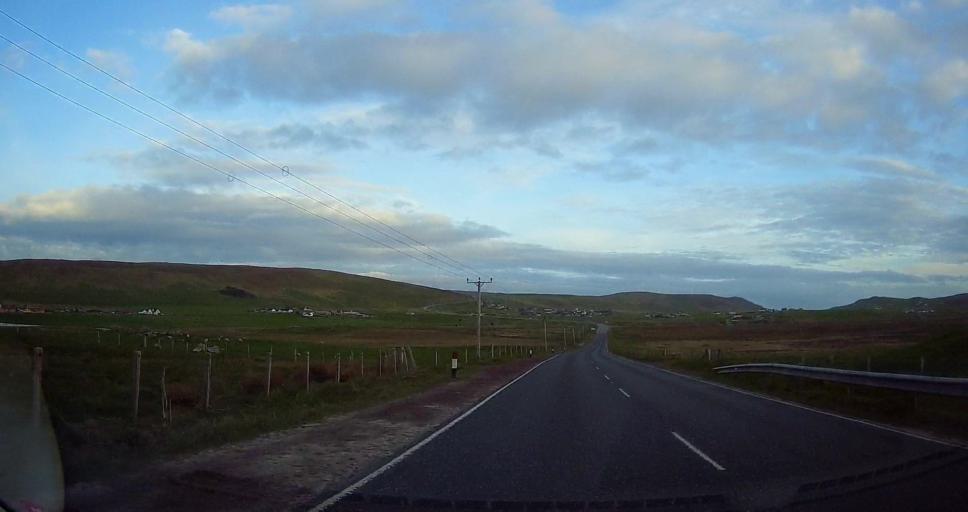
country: GB
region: Scotland
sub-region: Shetland Islands
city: Lerwick
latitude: 60.1977
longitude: -1.2320
